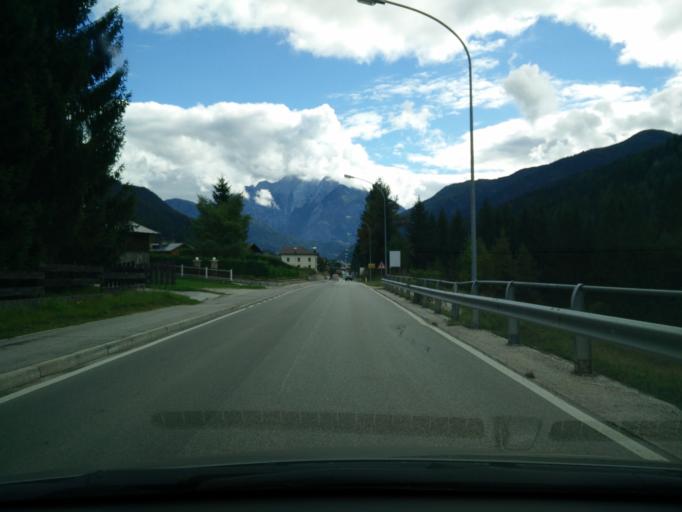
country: IT
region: Veneto
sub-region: Provincia di Belluno
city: Auronzo
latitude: 46.5664
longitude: 12.4067
